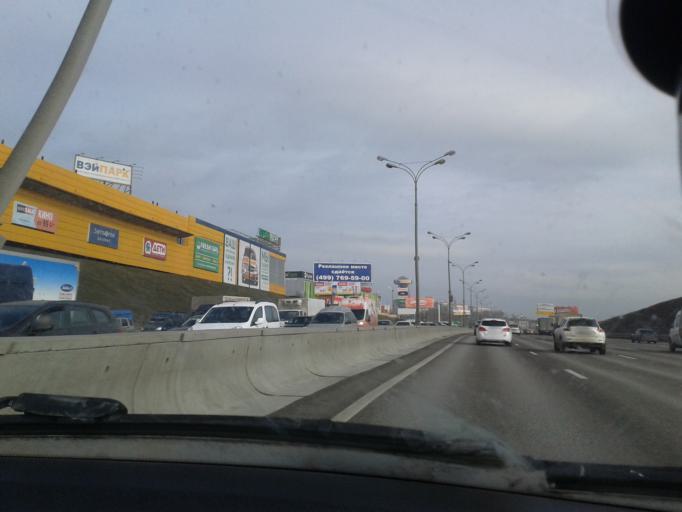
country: RU
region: Moscow
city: Strogino
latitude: 55.8573
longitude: 37.3969
